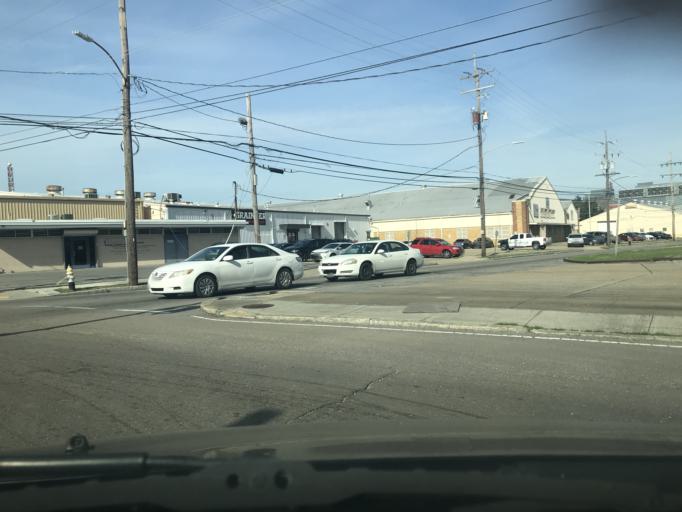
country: US
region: Louisiana
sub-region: Orleans Parish
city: New Orleans
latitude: 29.9560
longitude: -90.0877
